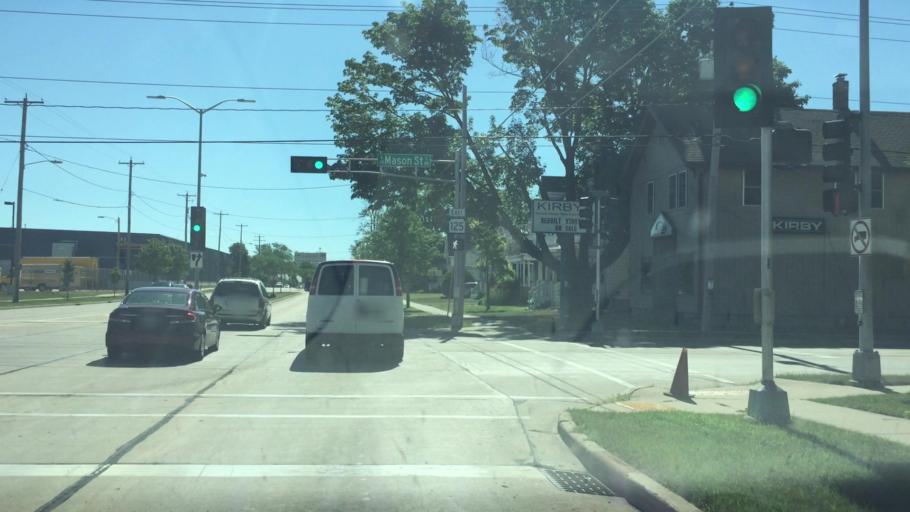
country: US
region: Wisconsin
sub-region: Outagamie County
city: Appleton
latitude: 44.2617
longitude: -88.4260
